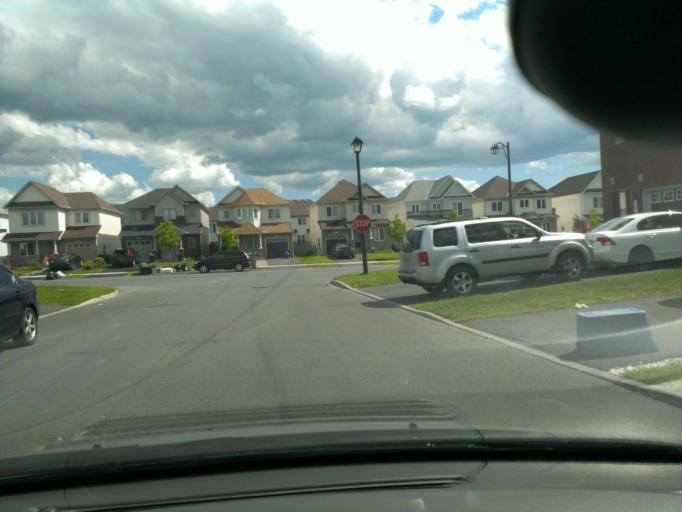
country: CA
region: Ontario
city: Clarence-Rockland
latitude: 45.4473
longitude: -75.4719
